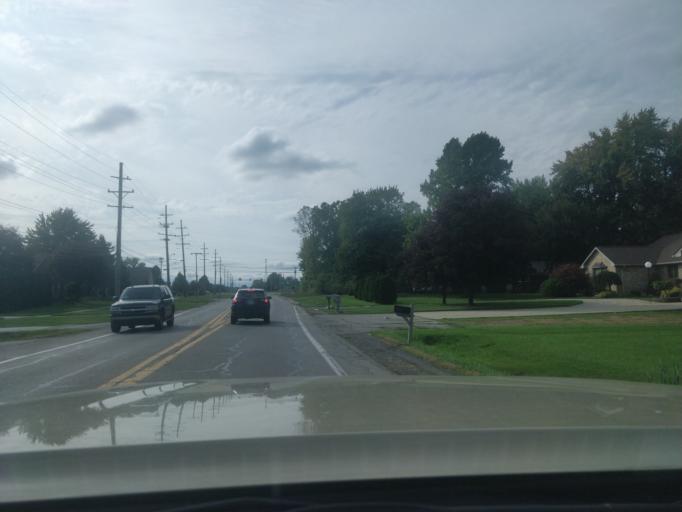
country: US
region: Michigan
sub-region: Wayne County
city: Woodhaven
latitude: 42.1541
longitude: -83.2501
